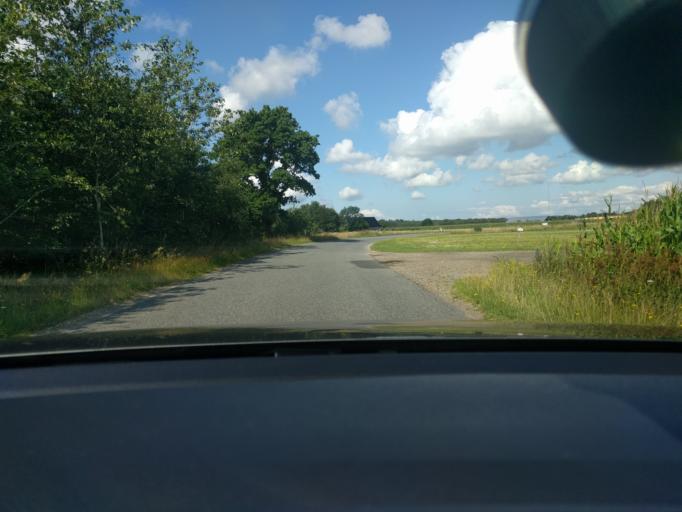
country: DK
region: Central Jutland
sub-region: Viborg Kommune
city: Viborg
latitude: 56.4409
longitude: 9.2969
